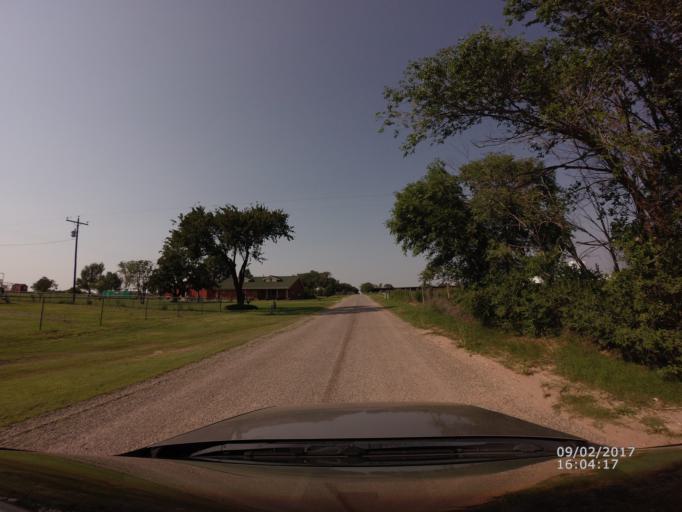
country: US
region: New Mexico
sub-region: Curry County
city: Clovis
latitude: 34.4435
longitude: -103.1996
